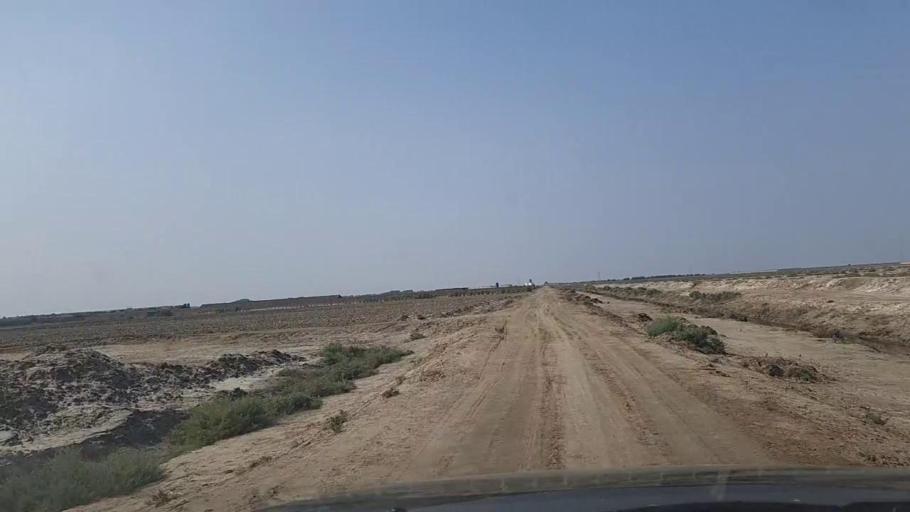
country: PK
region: Sindh
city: Gharo
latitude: 24.7047
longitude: 67.5702
